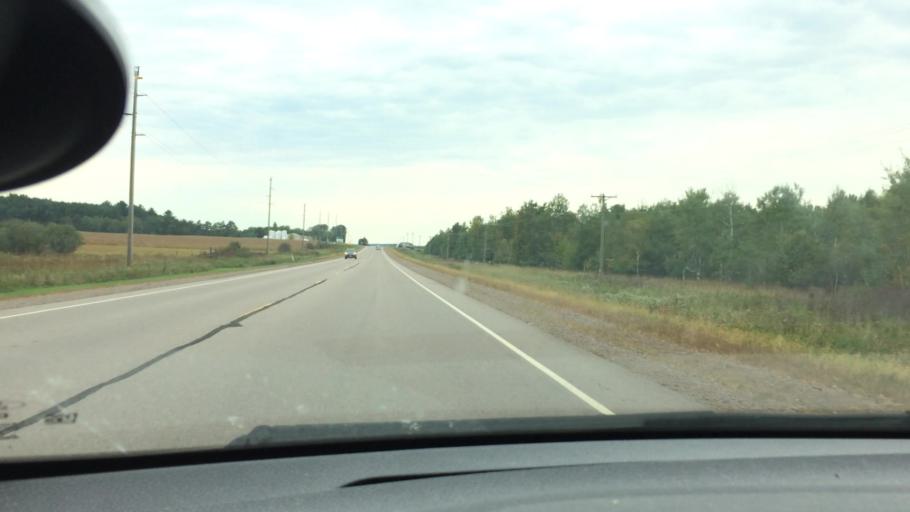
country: US
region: Wisconsin
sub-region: Eau Claire County
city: Augusta
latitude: 44.5964
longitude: -90.9258
